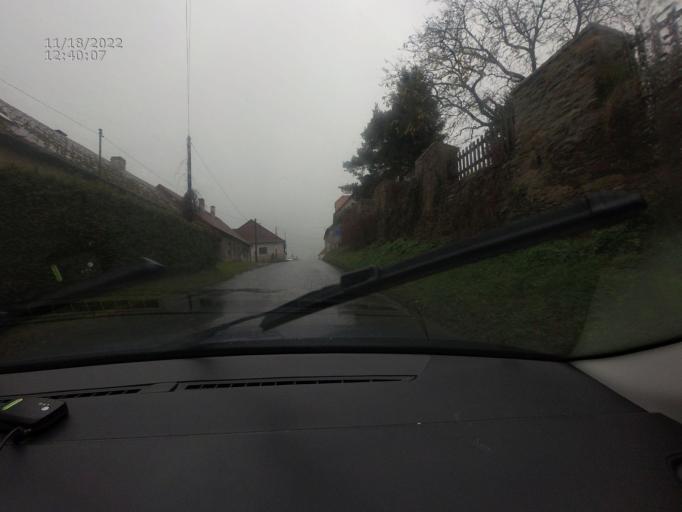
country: CZ
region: Plzensky
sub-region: Okres Klatovy
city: Planice
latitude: 49.3887
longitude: 13.4773
